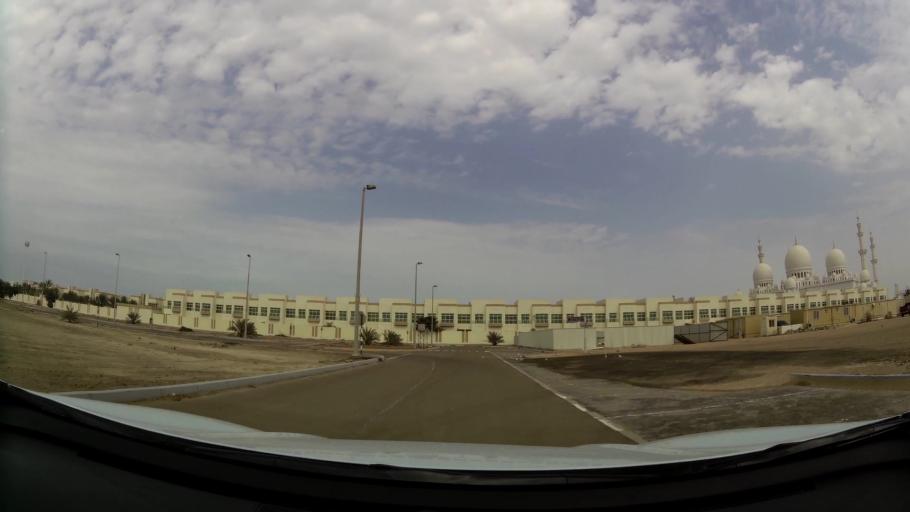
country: AE
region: Abu Dhabi
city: Abu Dhabi
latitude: 24.4101
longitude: 54.4700
